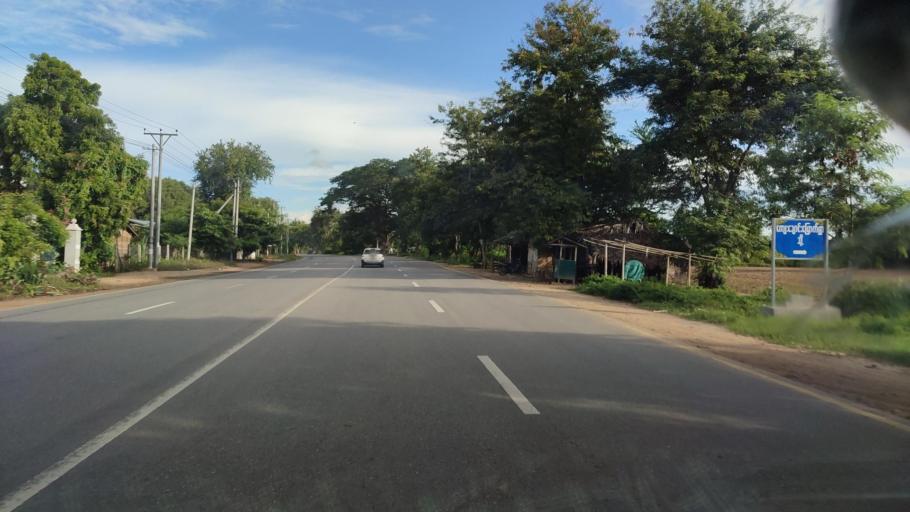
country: MM
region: Mandalay
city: Yamethin
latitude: 20.1879
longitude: 96.1858
